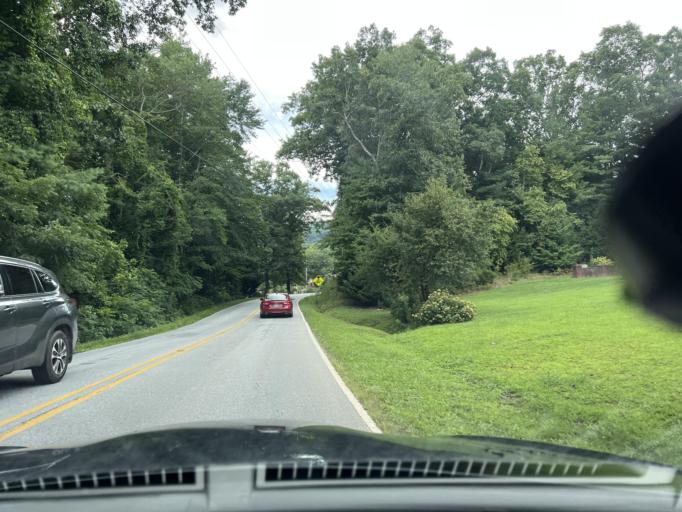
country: US
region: North Carolina
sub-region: Henderson County
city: Hoopers Creek
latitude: 35.4387
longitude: -82.4470
